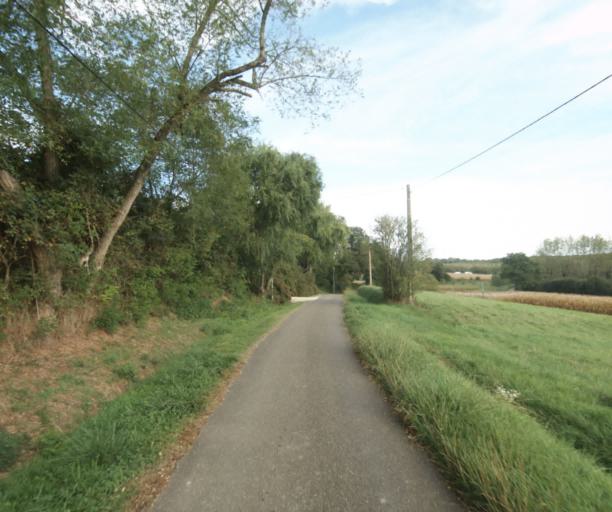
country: FR
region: Midi-Pyrenees
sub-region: Departement du Gers
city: Cazaubon
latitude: 43.8672
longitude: -0.1230
